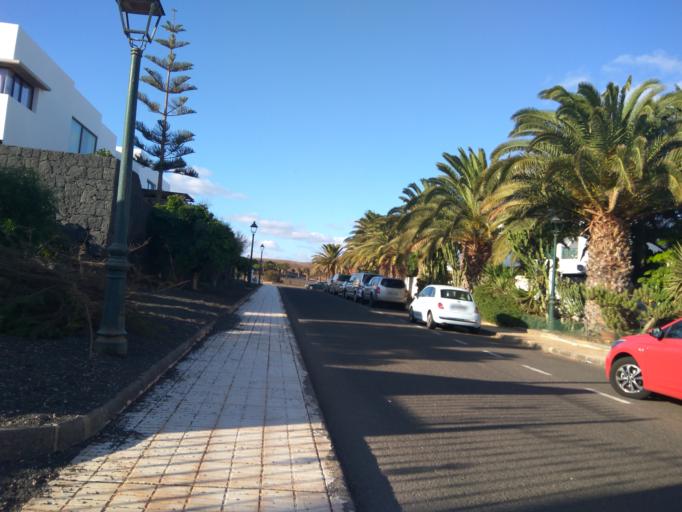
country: ES
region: Canary Islands
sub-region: Provincia de Las Palmas
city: Arrecife
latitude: 29.0067
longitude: -13.4877
